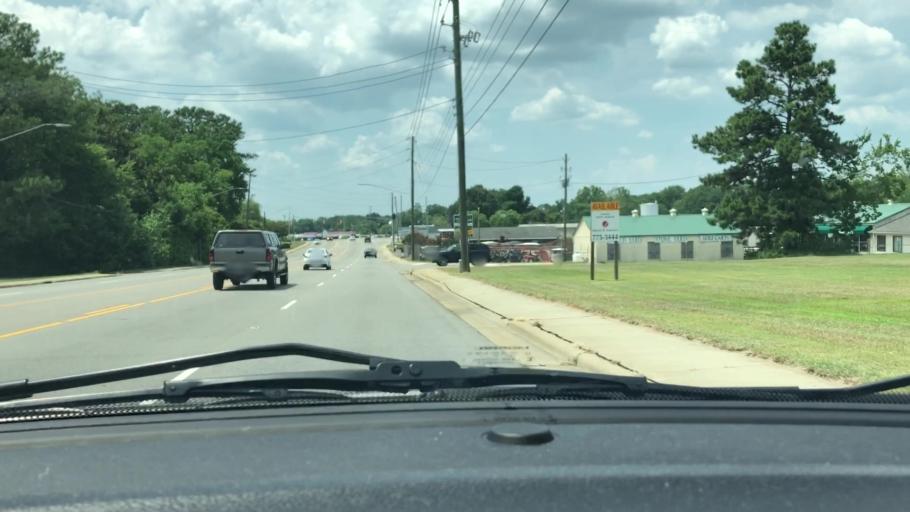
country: US
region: North Carolina
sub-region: Lee County
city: Sanford
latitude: 35.4688
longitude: -79.1642
